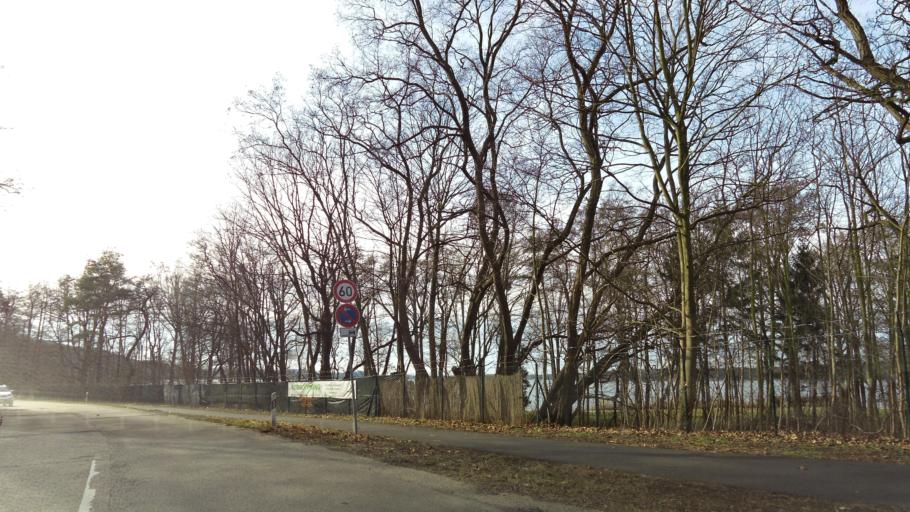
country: DE
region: Brandenburg
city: Michendorf
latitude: 52.3590
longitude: 13.0219
